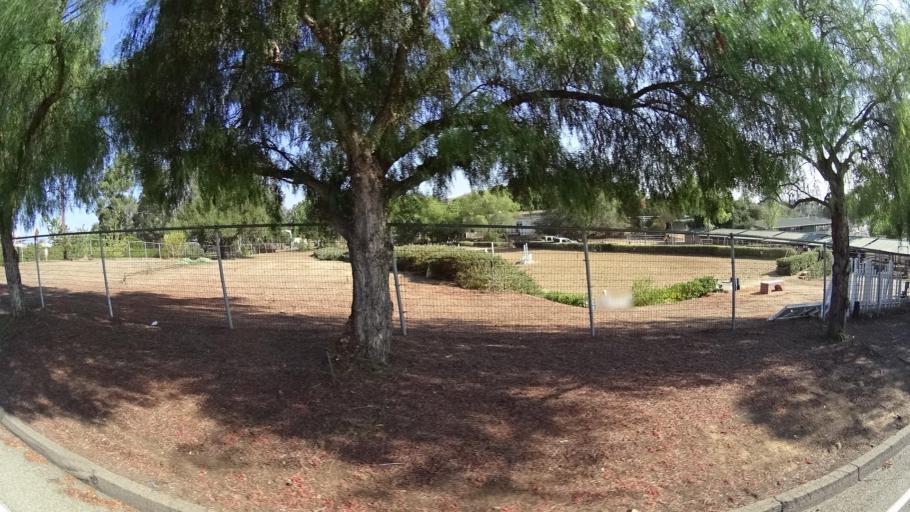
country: US
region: California
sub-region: San Diego County
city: Bonsall
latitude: 33.3219
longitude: -117.2552
